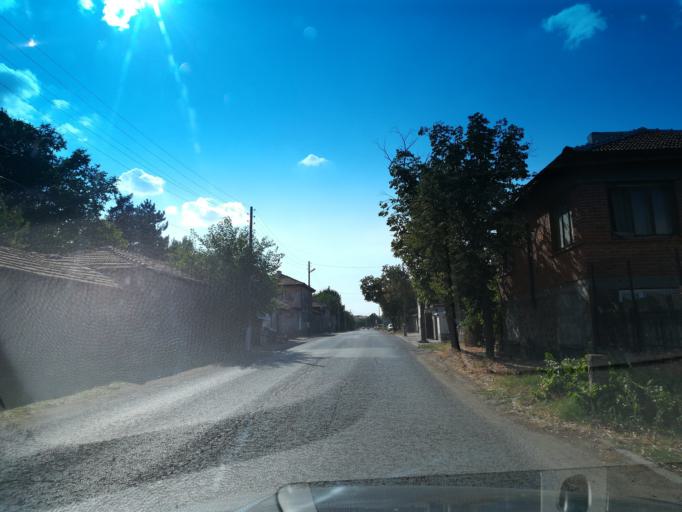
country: BG
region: Khaskovo
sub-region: Obshtina Mineralni Bani
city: Mineralni Bani
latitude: 42.0163
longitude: 25.4256
